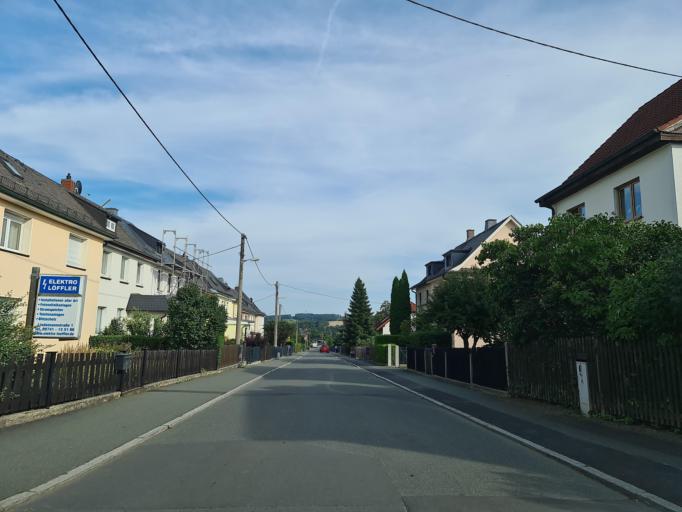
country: DE
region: Saxony
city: Plauen
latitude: 50.4890
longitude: 12.0990
